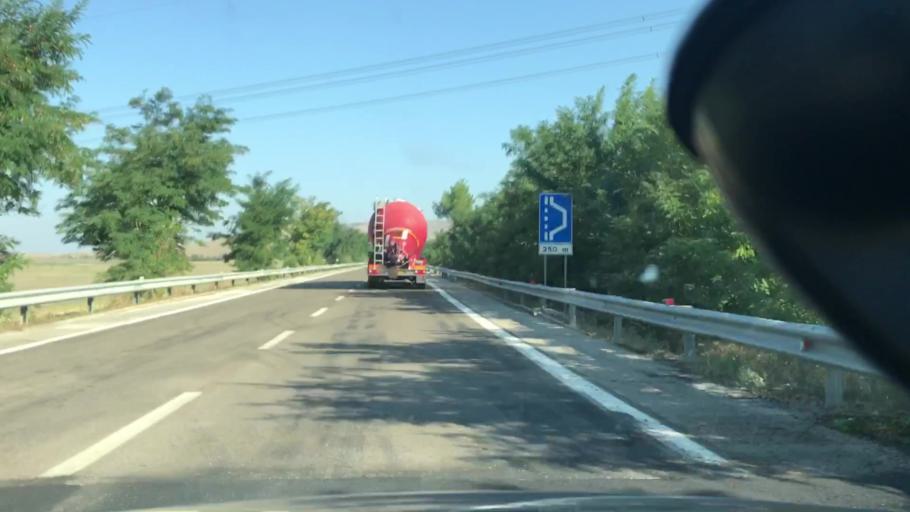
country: IT
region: Basilicate
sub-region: Provincia di Matera
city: Irsina
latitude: 40.7996
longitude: 16.2747
